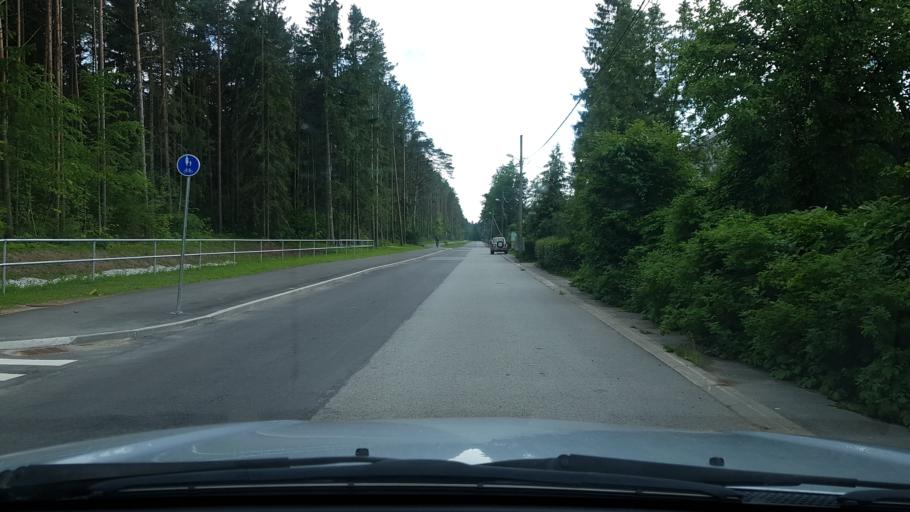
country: EE
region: Ida-Virumaa
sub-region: Narva-Joesuu linn
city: Narva-Joesuu
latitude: 59.4526
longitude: 28.0336
